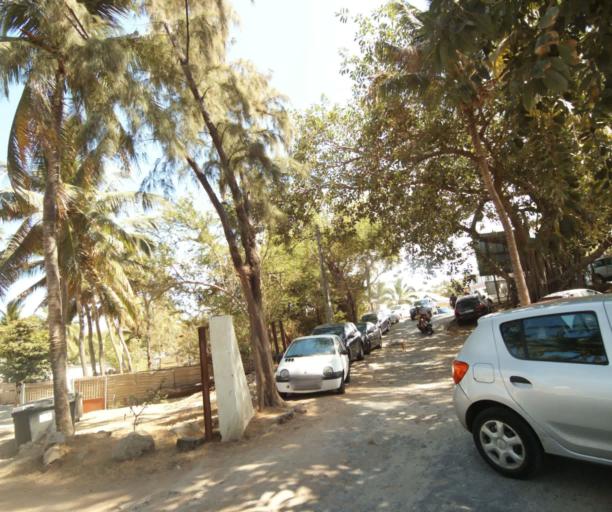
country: RE
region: Reunion
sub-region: Reunion
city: Trois-Bassins
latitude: -21.1006
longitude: 55.2437
